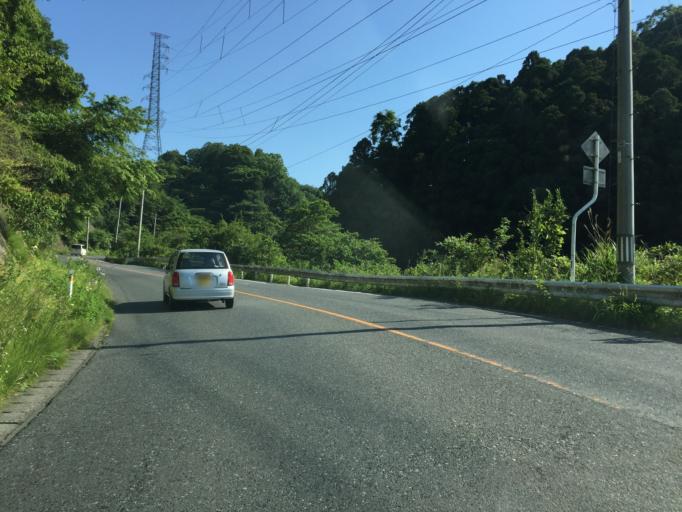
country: JP
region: Fukushima
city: Iwaki
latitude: 36.9523
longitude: 140.8275
